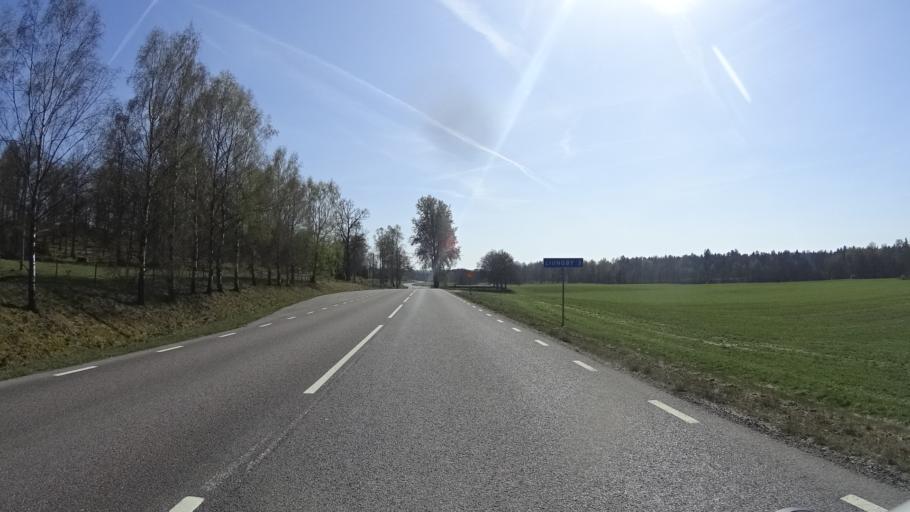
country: SE
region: Kronoberg
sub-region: Ljungby Kommun
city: Ljungby
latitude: 56.8494
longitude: 13.9766
